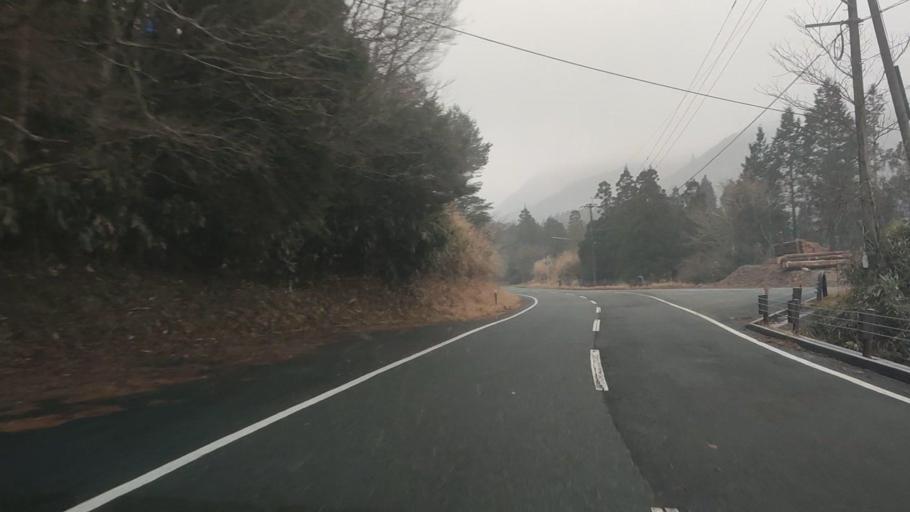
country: JP
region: Kumamoto
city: Matsubase
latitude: 32.5717
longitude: 130.9070
